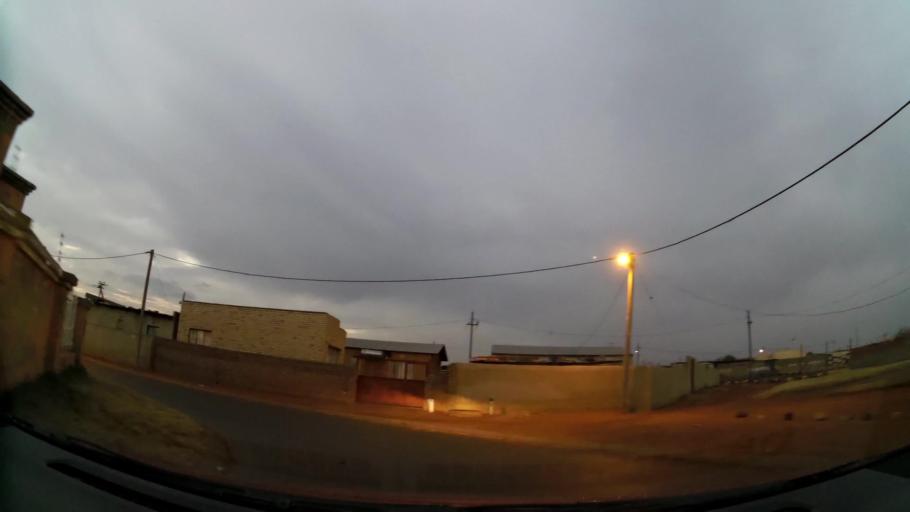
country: ZA
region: Gauteng
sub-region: West Rand District Municipality
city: Randfontein
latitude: -26.1749
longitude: 27.7861
